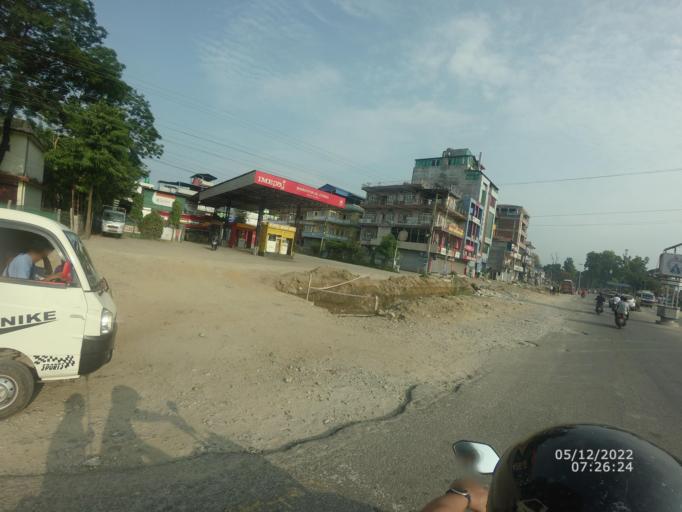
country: NP
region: Central Region
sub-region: Narayani Zone
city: Bharatpur
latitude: 27.6846
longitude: 84.4296
